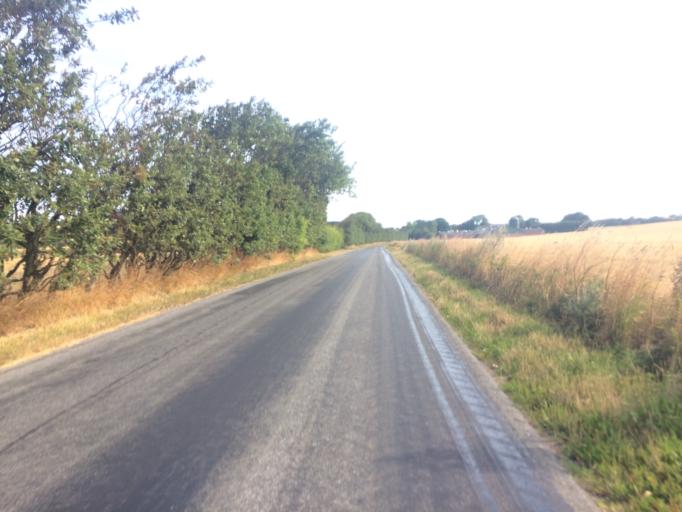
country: DK
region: Central Jutland
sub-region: Holstebro Kommune
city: Vinderup
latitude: 56.5960
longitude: 8.7579
